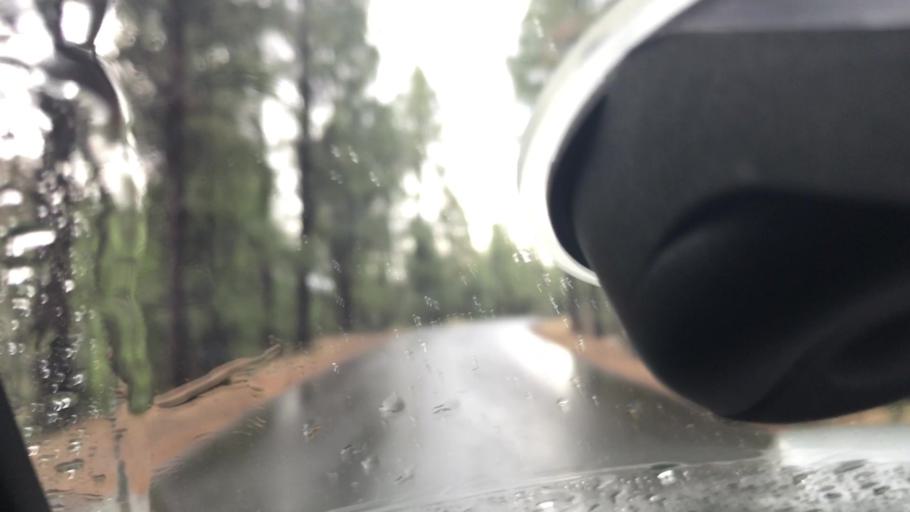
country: US
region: Arizona
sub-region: Yavapai County
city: Prescott
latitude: 34.5145
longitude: -112.3814
